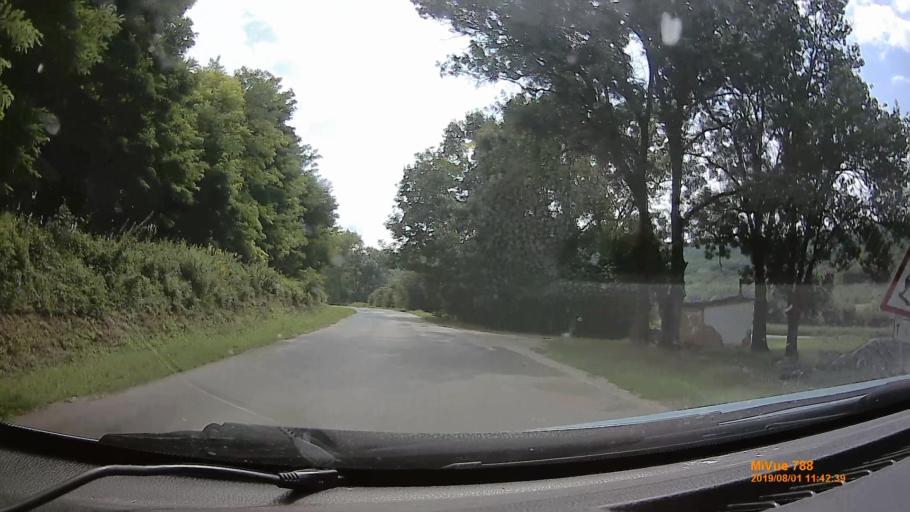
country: HU
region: Baranya
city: Villany
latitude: 45.8834
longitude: 18.4118
